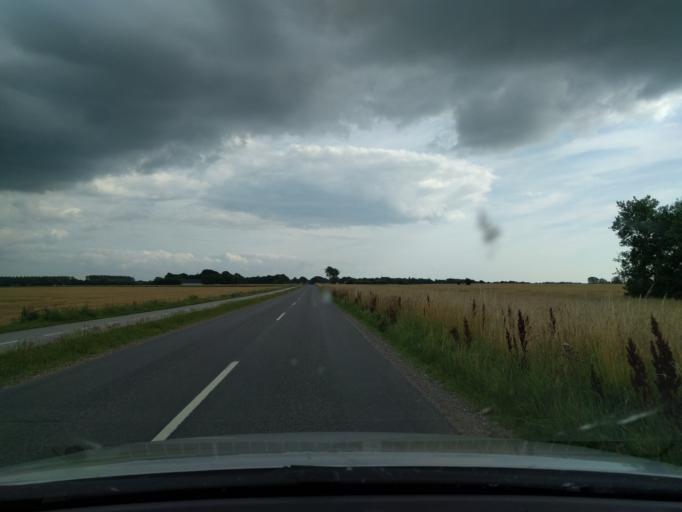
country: DK
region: Central Jutland
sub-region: Herning Kommune
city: Snejbjerg
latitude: 56.1006
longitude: 8.9098
